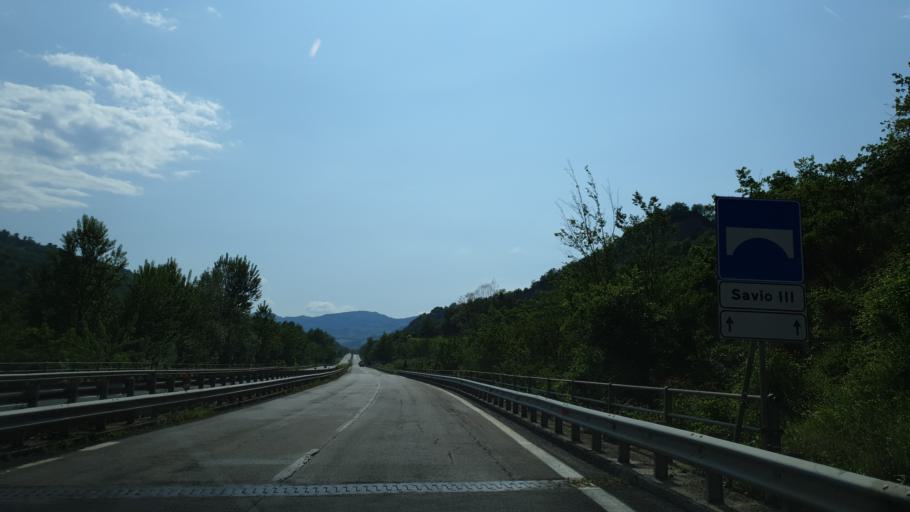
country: IT
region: Emilia-Romagna
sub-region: Forli-Cesena
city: San Piero in Bagno
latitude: 43.8911
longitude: 12.0430
